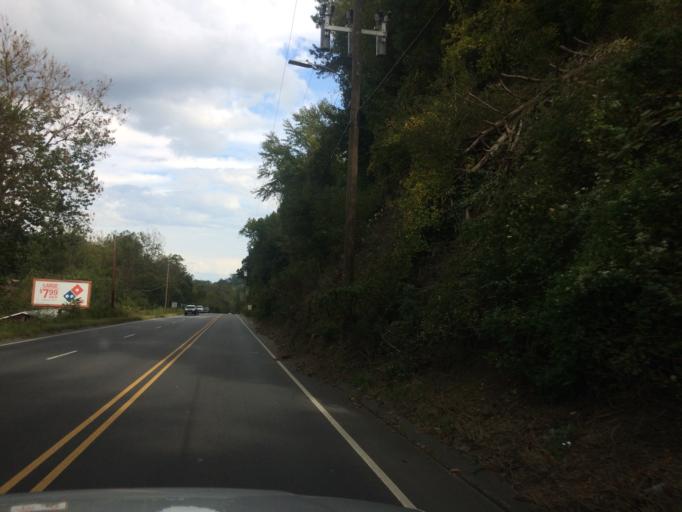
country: US
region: North Carolina
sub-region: Haywood County
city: Canton
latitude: 35.5345
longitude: -82.8297
